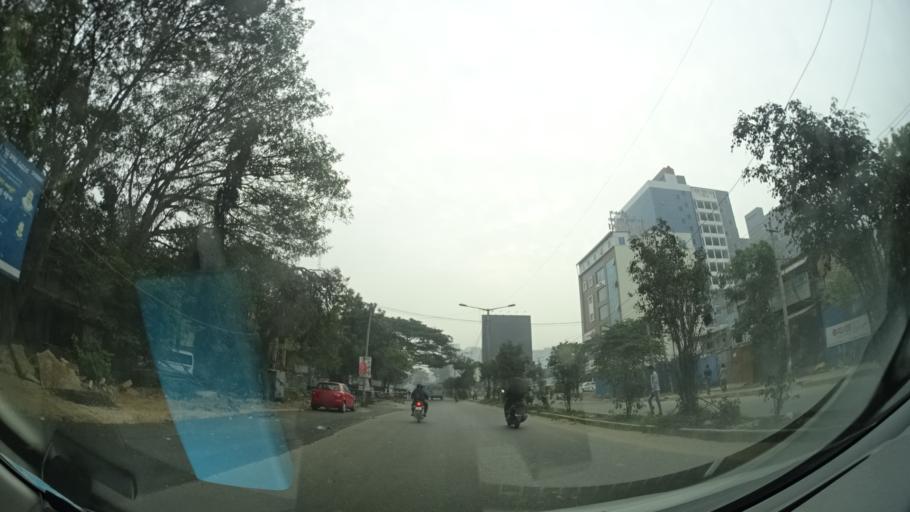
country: IN
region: Karnataka
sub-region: Bangalore Urban
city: Bangalore
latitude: 12.9949
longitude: 77.6986
